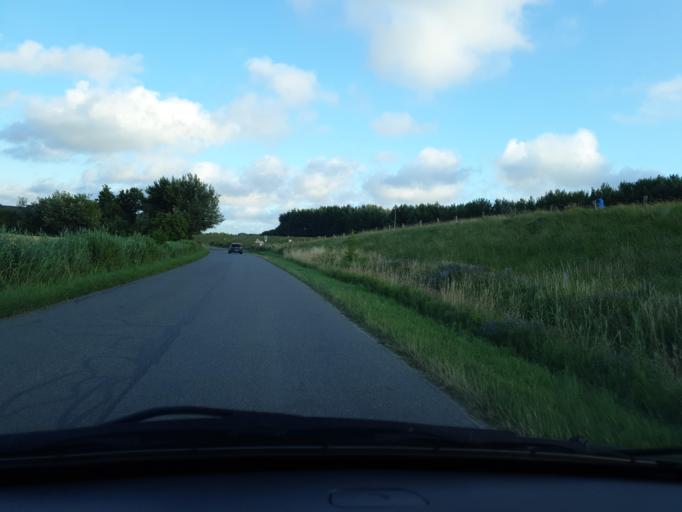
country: DE
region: Schleswig-Holstein
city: Elpersbuttel
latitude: 54.0697
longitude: 9.0140
